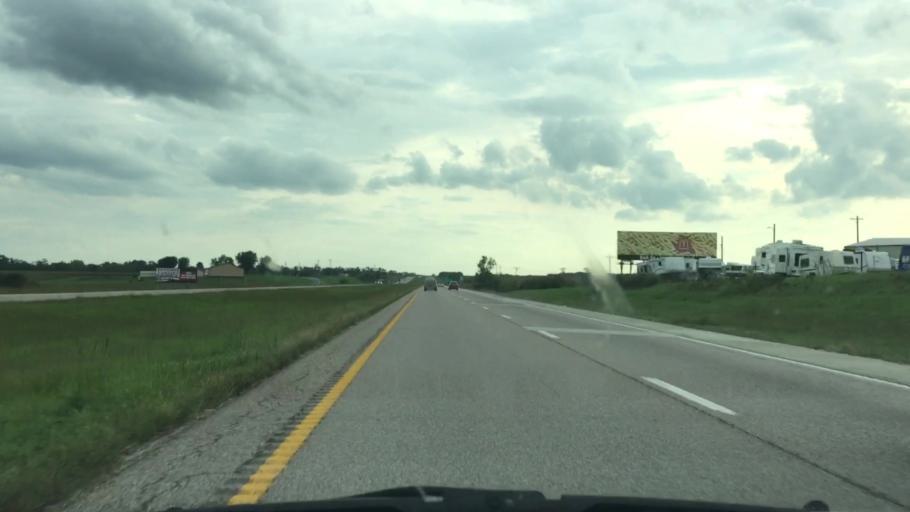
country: US
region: Missouri
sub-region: Clinton County
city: Lathrop
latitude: 39.5459
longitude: -94.2723
